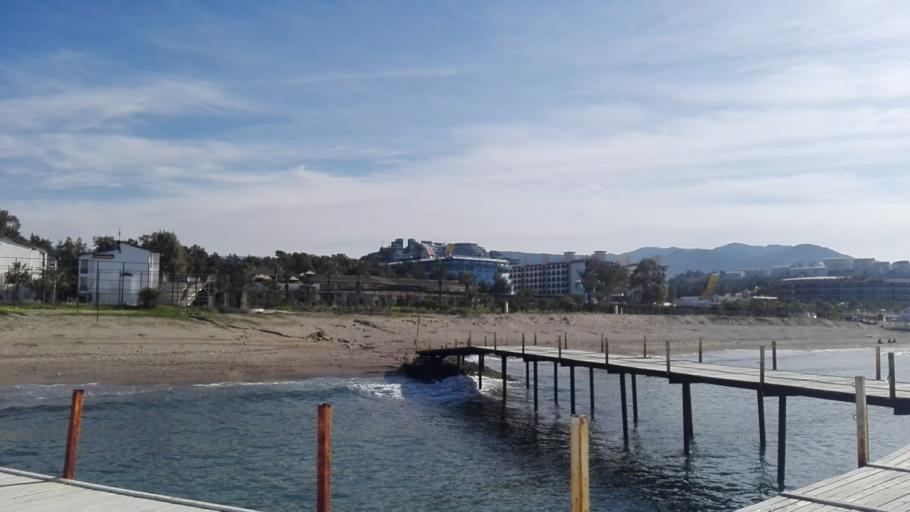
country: TR
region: Antalya
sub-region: Alanya
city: Payallar
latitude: 36.5782
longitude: 31.8817
